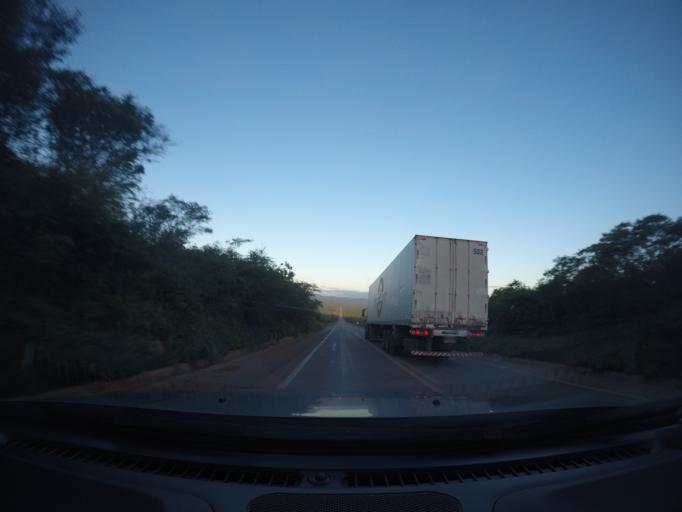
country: BR
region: Bahia
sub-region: Seabra
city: Seabra
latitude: -12.4129
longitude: -41.9759
